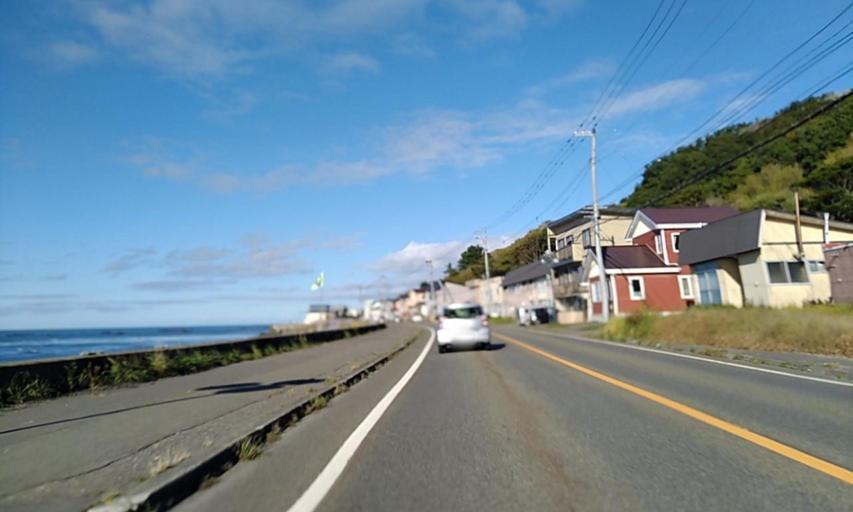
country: JP
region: Hokkaido
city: Shizunai-furukawacho
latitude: 42.1770
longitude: 142.7414
